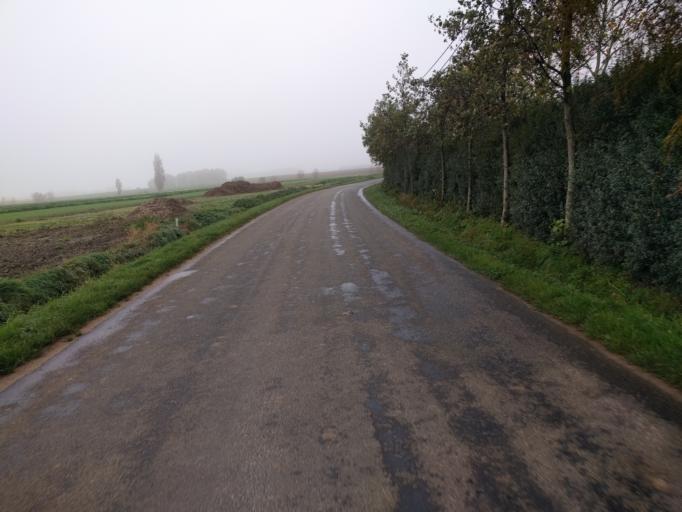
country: BE
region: Flanders
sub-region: Provincie West-Vlaanderen
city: Poperinge
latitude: 50.8203
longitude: 2.7990
